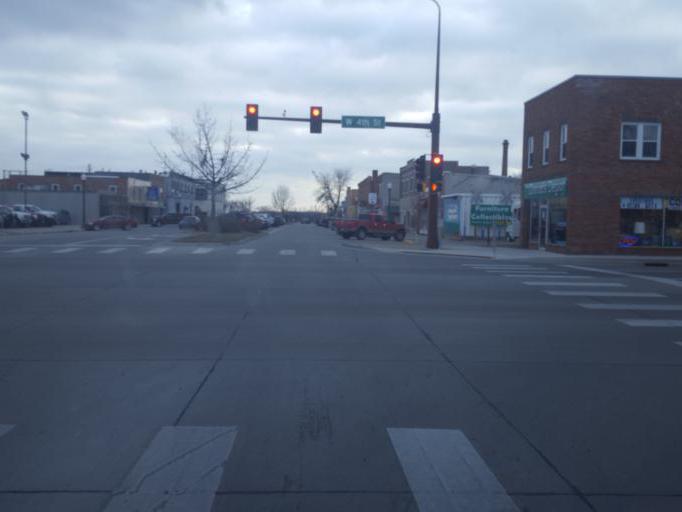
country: US
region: South Dakota
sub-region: Yankton County
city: Yankton
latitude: 42.8713
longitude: -97.3923
